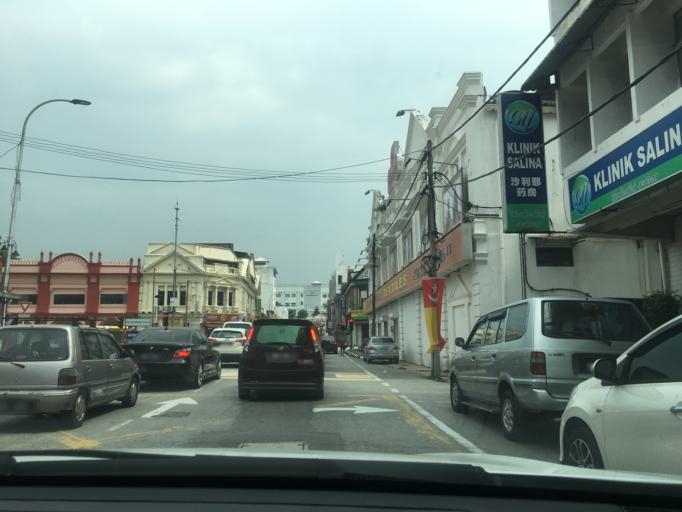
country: MY
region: Selangor
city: Klang
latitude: 3.0424
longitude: 101.4472
